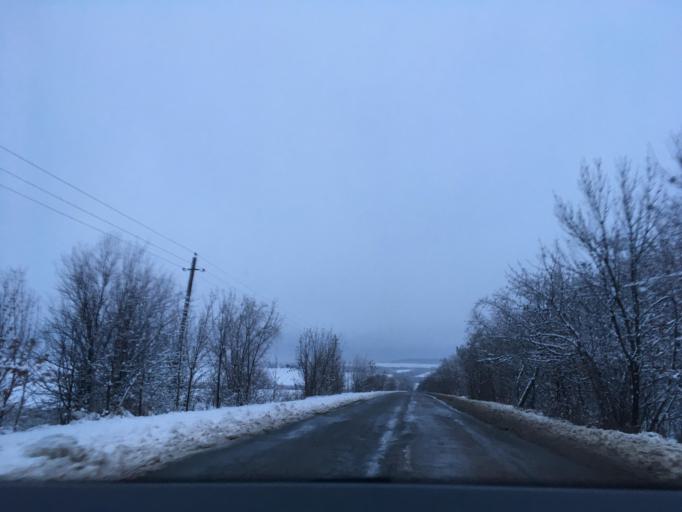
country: RU
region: Voronezj
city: Verkhniy Mamon
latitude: 50.0485
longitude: 40.2413
